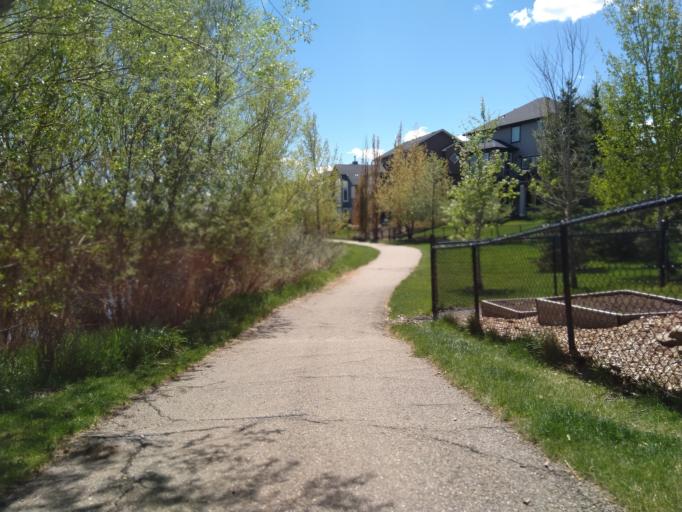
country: CA
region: Alberta
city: Chestermere
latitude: 51.0284
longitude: -113.8357
